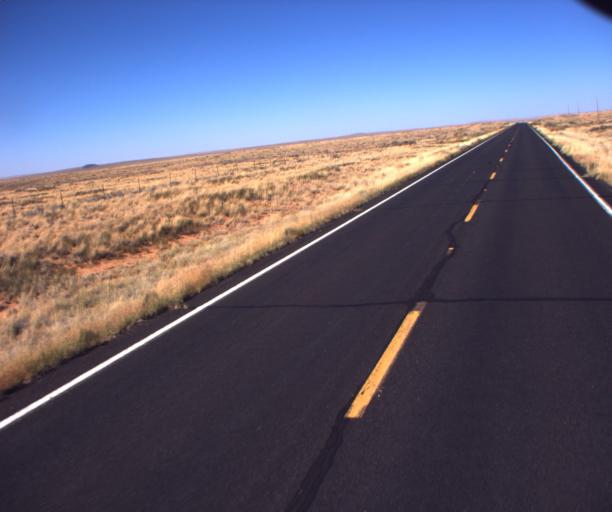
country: US
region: Arizona
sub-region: Navajo County
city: Dilkon
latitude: 35.5442
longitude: -110.4504
